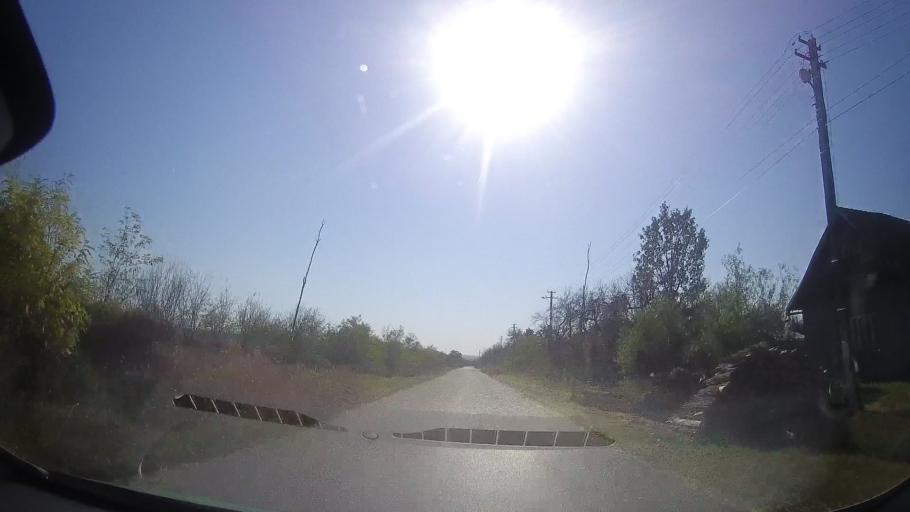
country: RO
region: Timis
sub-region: Comuna Ghizela
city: Ghizela
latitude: 45.8271
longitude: 21.7500
